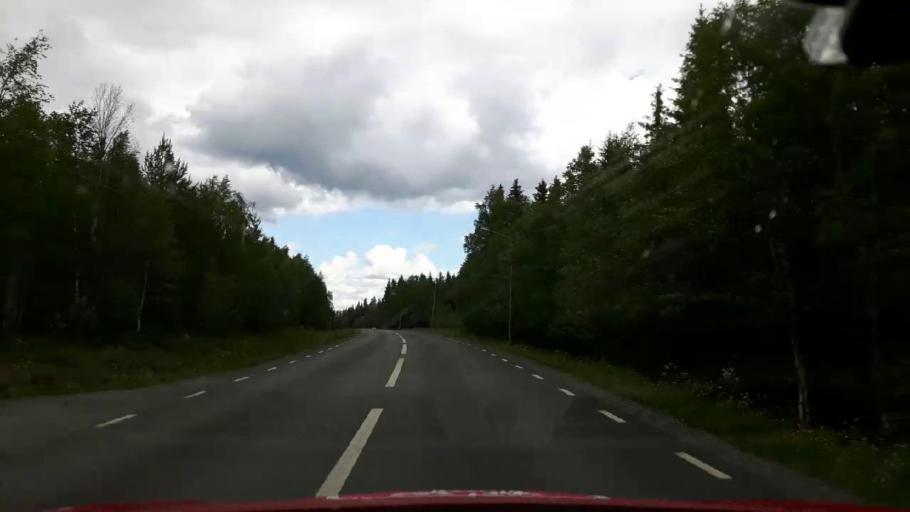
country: SE
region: Jaemtland
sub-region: Krokoms Kommun
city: Krokom
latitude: 63.7513
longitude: 14.2959
